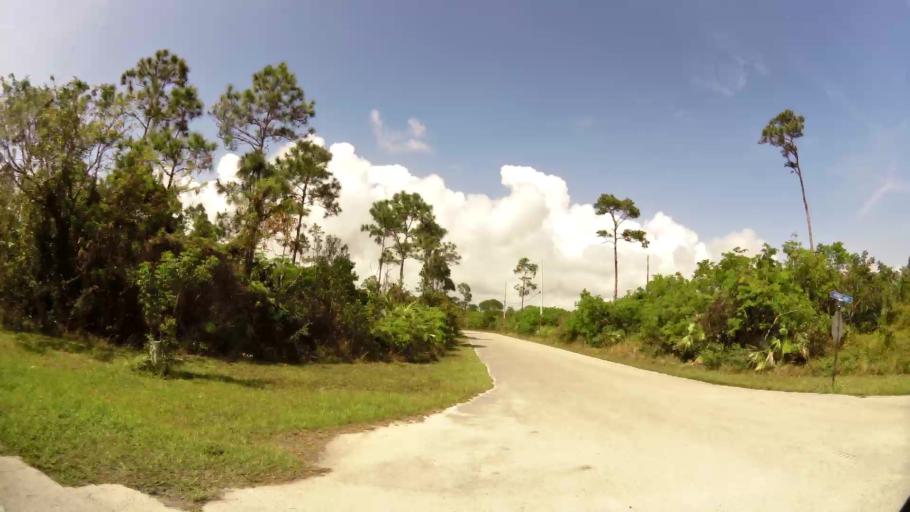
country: BS
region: Freeport
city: Freeport
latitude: 26.4994
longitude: -78.7044
